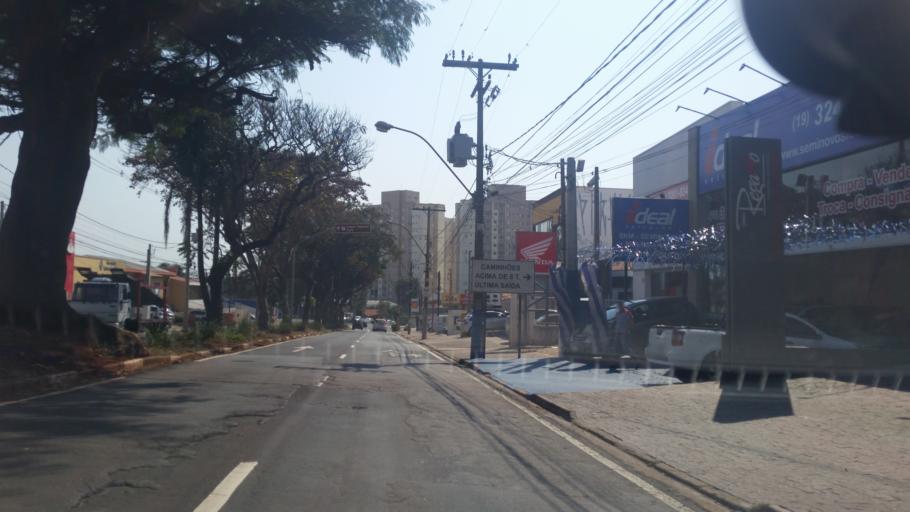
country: BR
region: Sao Paulo
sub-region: Campinas
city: Campinas
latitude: -22.8826
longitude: -47.0730
